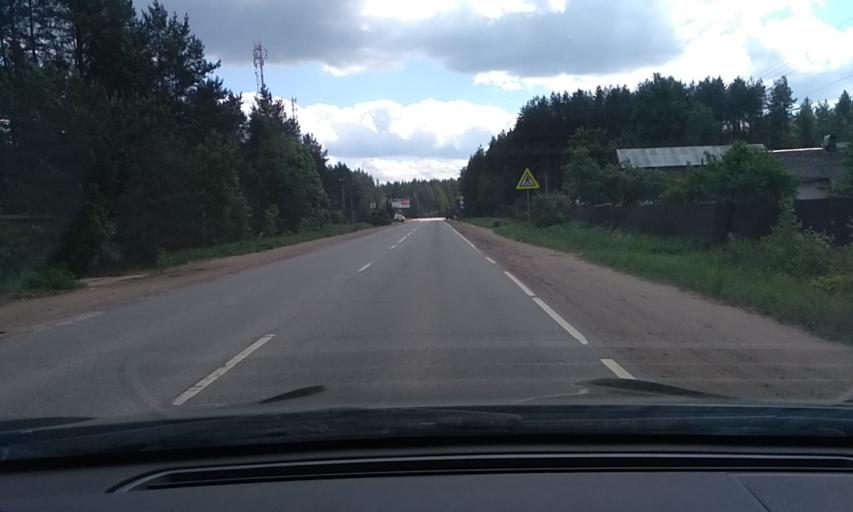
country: RU
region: Leningrad
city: Imeni Sverdlova
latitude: 59.8615
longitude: 30.6713
